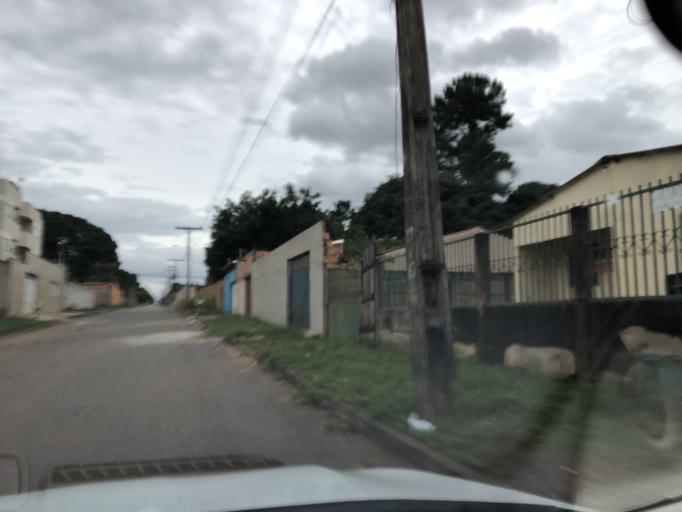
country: BR
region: Goias
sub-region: Luziania
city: Luziania
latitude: -16.1561
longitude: -47.9477
